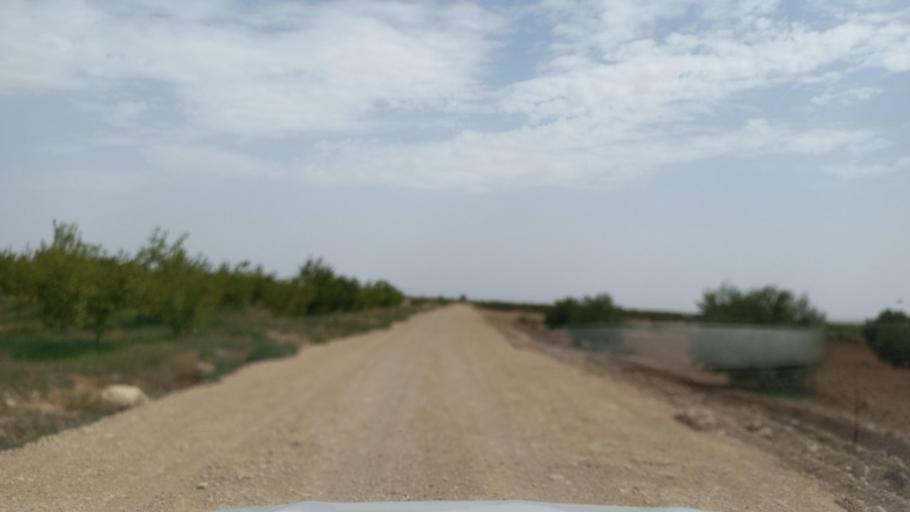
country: TN
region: Al Qasrayn
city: Kasserine
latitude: 35.2780
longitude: 9.0184
